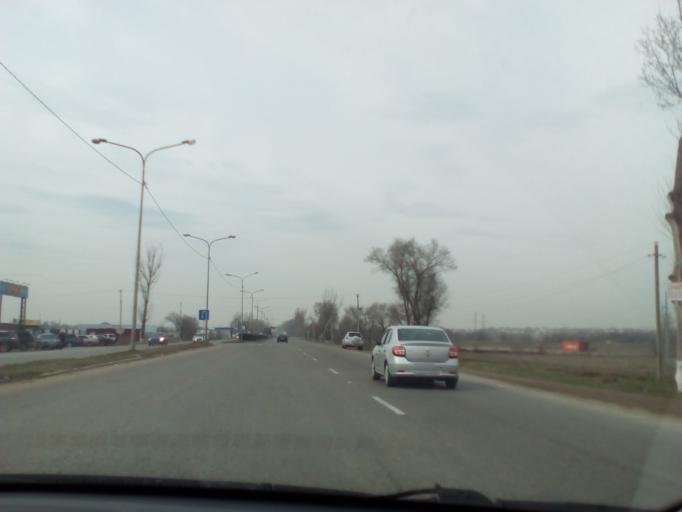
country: KZ
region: Almaty Oblysy
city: Burunday
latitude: 43.2210
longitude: 76.6279
